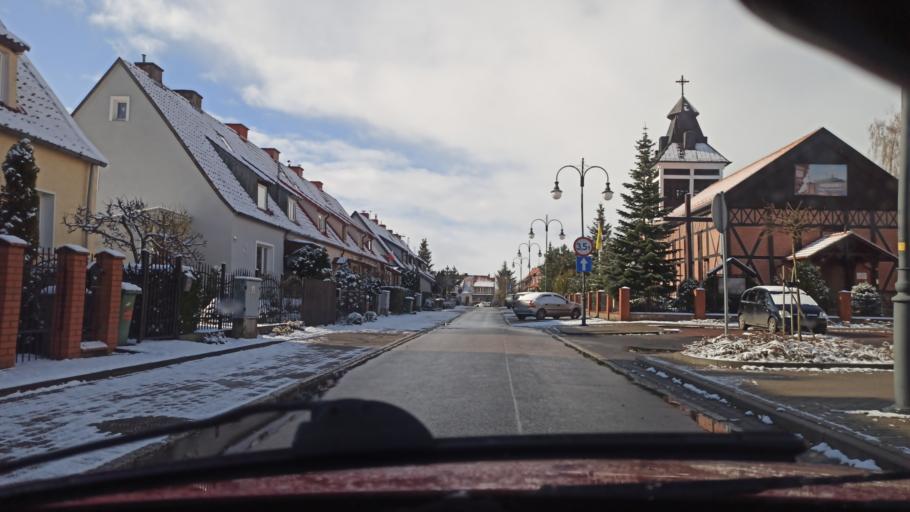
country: PL
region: Warmian-Masurian Voivodeship
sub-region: Powiat elblaski
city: Elblag
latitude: 54.1448
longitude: 19.4073
